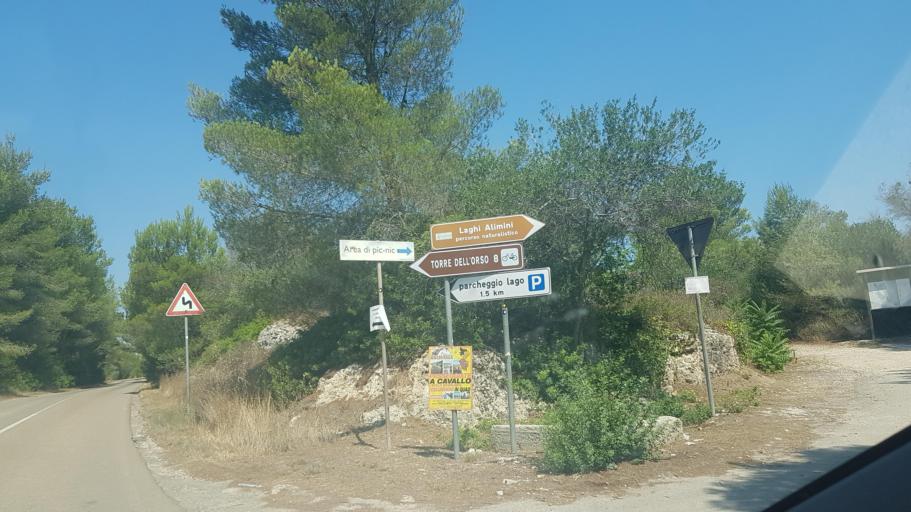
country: IT
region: Apulia
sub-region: Provincia di Lecce
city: Otranto
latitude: 40.1908
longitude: 18.4453
